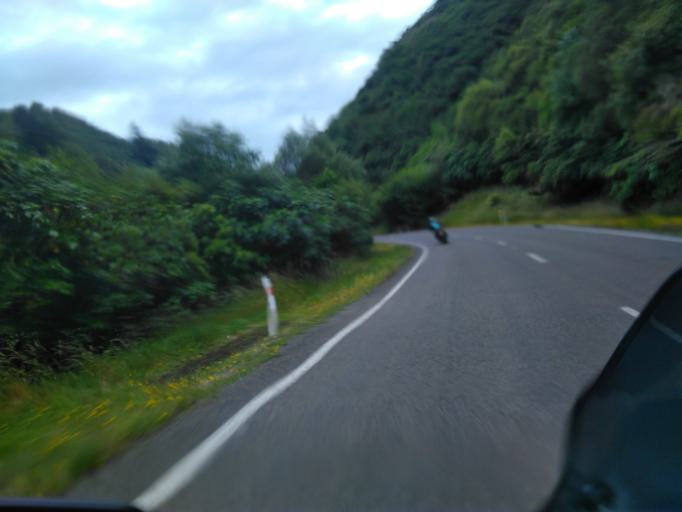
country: NZ
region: Bay of Plenty
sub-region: Opotiki District
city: Opotiki
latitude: -38.3413
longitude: 177.4312
